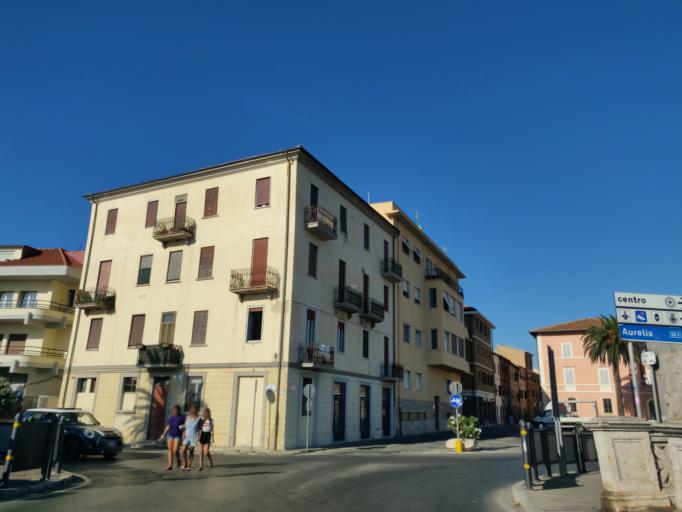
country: IT
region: Tuscany
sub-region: Provincia di Grosseto
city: Orbetello
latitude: 42.4364
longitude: 11.2069
